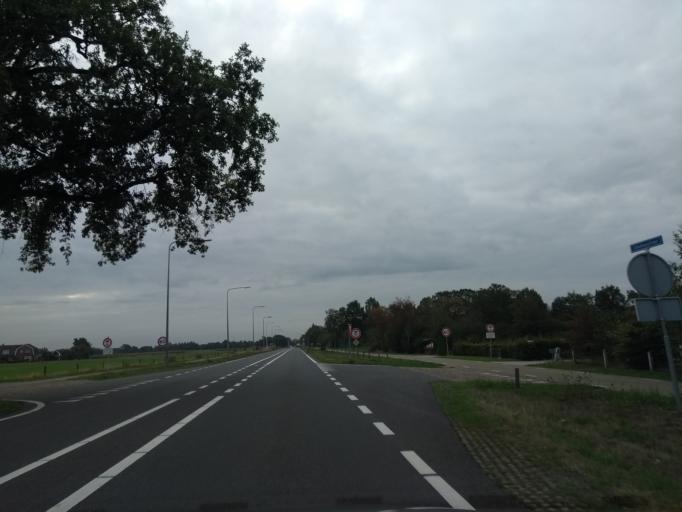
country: NL
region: Overijssel
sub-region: Gemeente Almelo
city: Almelo
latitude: 52.3341
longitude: 6.7042
